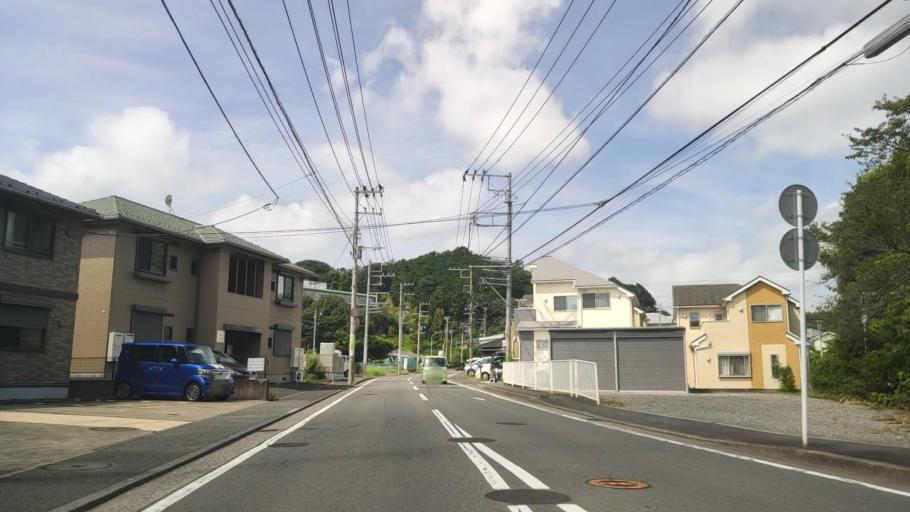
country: JP
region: Kanagawa
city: Minami-rinkan
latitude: 35.4325
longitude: 139.5313
